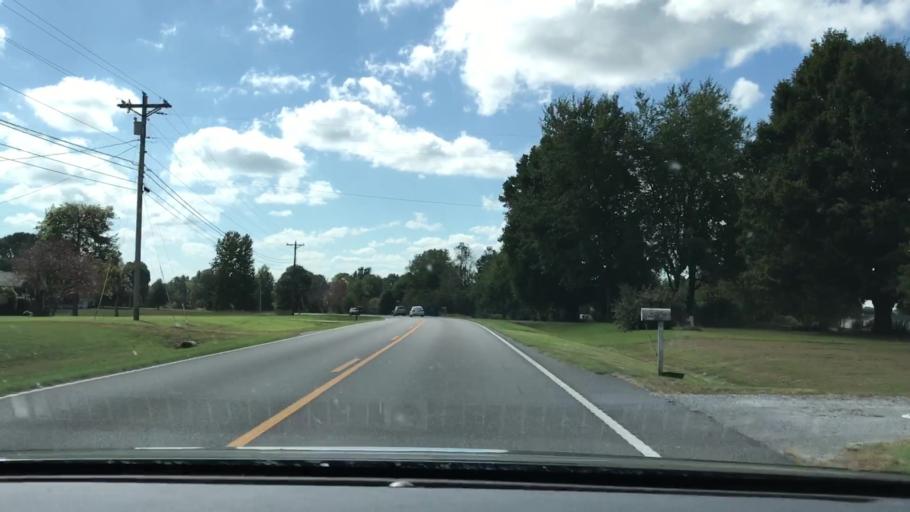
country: US
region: Kentucky
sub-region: McCracken County
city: Reidland
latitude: 36.9827
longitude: -88.5159
